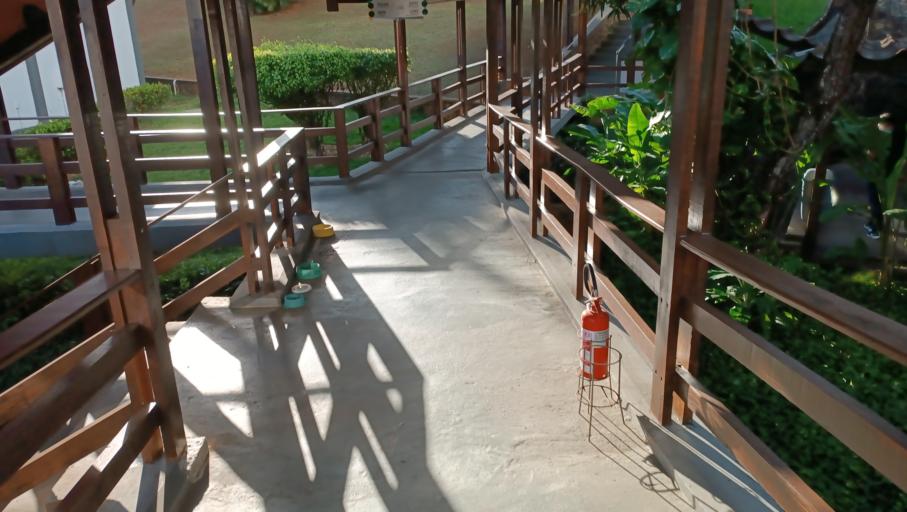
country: BR
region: Bahia
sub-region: Salvador
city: Salvador
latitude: -12.9581
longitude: -38.4399
